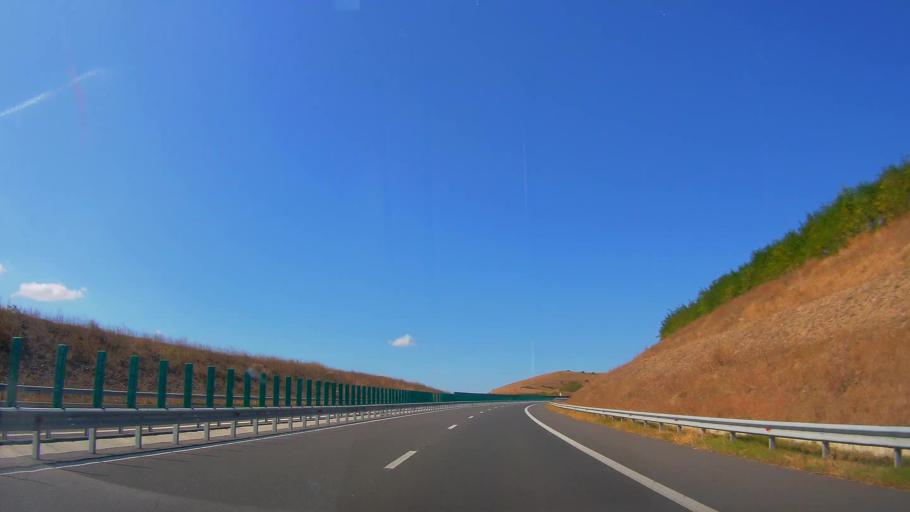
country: RO
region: Cluj
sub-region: Comuna Gilau
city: Gilau
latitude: 46.7629
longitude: 23.3900
